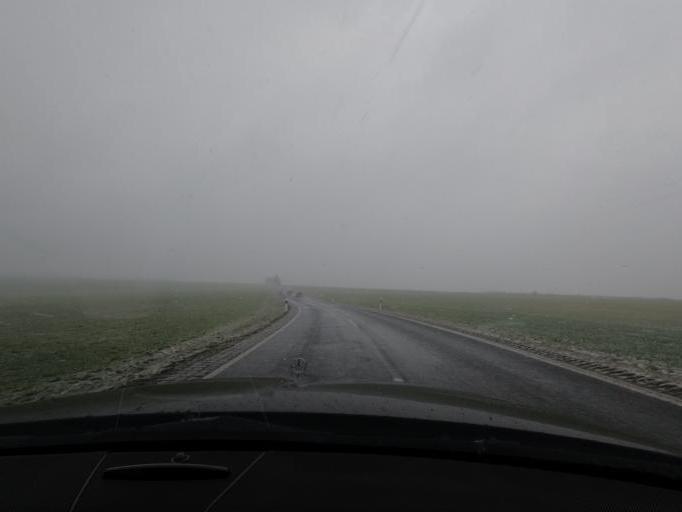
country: DE
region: Thuringia
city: Kullstedt
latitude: 51.2599
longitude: 10.2770
